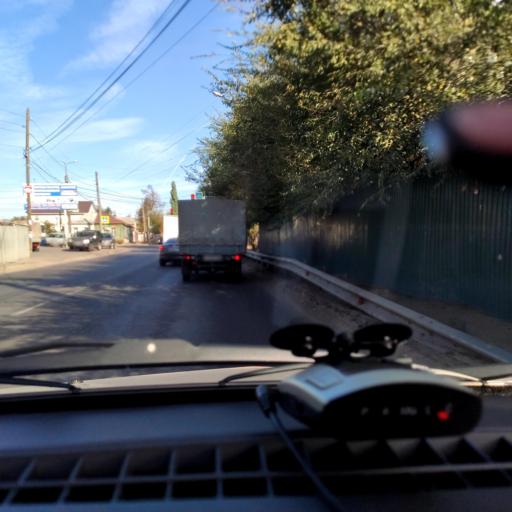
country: RU
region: Voronezj
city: Voronezh
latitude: 51.6937
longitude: 39.1646
